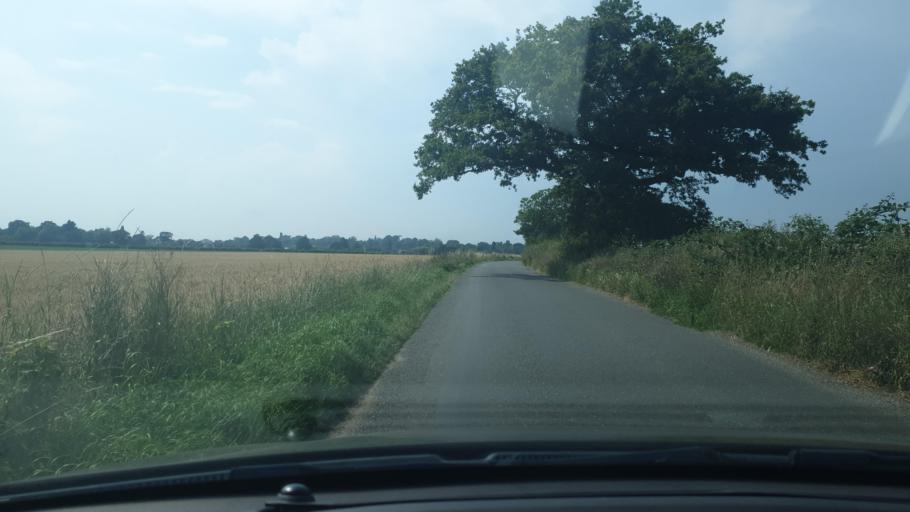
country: GB
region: England
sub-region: Suffolk
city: East Bergholt
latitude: 51.9531
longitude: 1.0088
